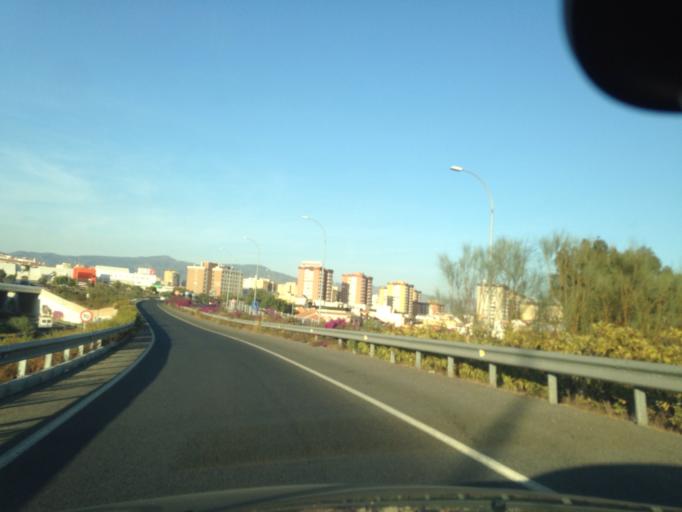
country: ES
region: Andalusia
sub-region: Provincia de Malaga
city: Malaga
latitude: 36.7119
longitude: -4.4572
